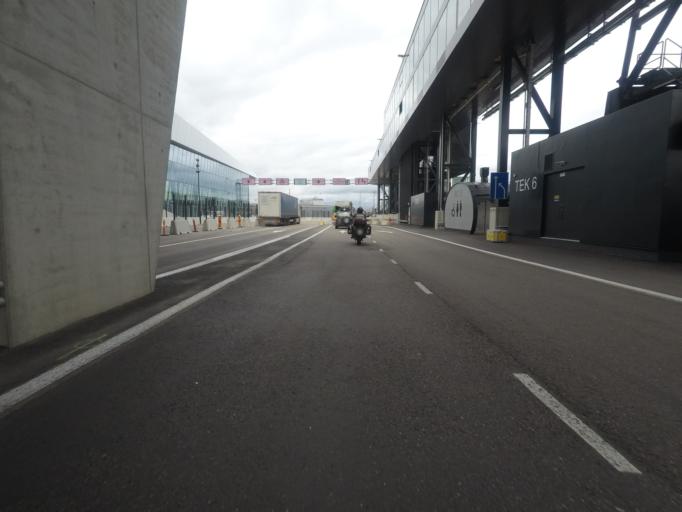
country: FI
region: Uusimaa
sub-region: Helsinki
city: Helsinki
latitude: 60.1492
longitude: 24.9150
